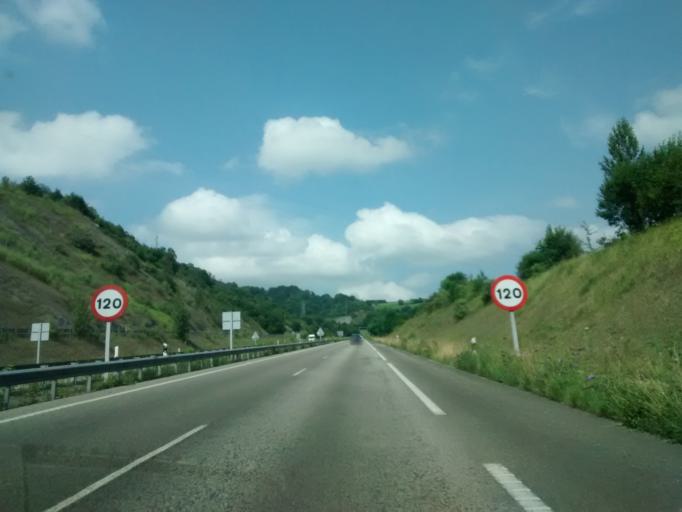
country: ES
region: Asturias
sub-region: Province of Asturias
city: Sama
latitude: 43.3333
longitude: -5.7183
